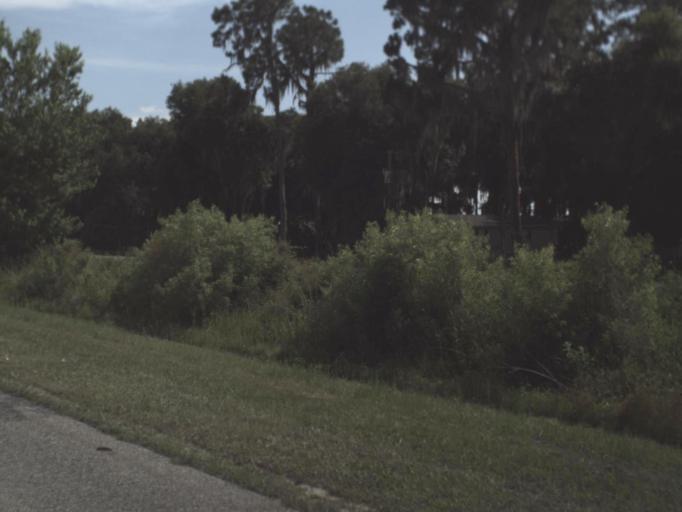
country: US
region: Florida
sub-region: Alachua County
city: Hawthorne
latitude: 29.5146
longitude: -82.1016
